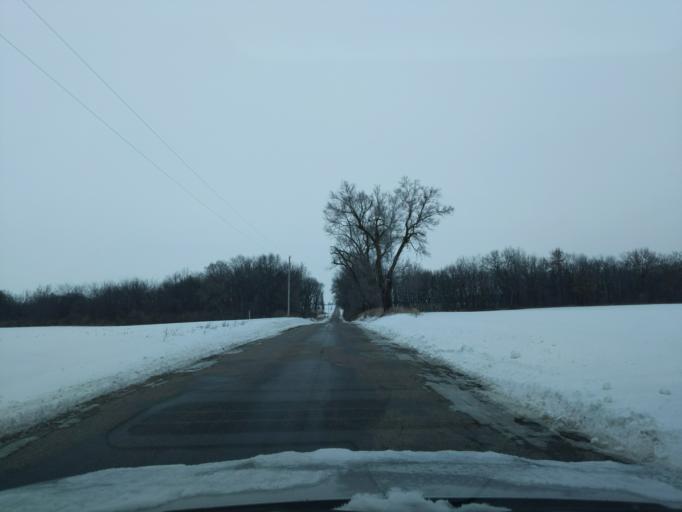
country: US
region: Indiana
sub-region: Benton County
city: Otterbein
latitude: 40.4176
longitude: -87.0895
